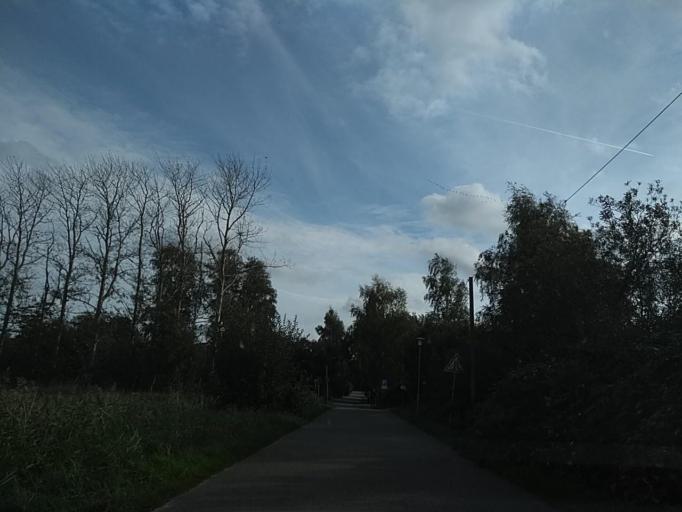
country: DE
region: Mecklenburg-Vorpommern
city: Seeheilbad Graal-Muritz
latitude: 54.2595
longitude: 12.2550
